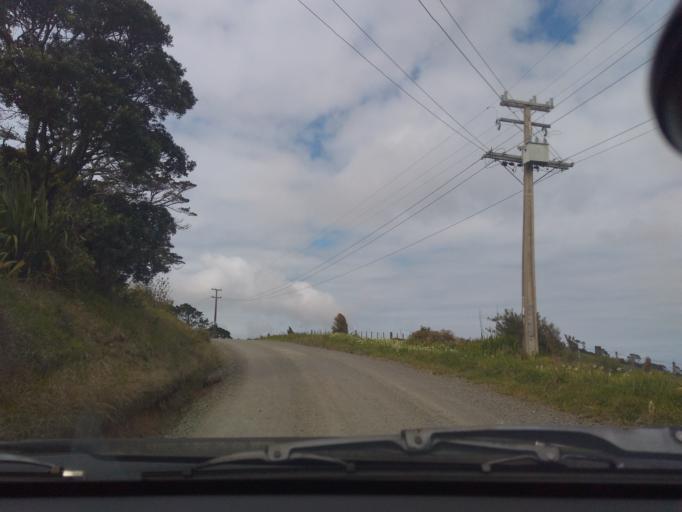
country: NZ
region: Auckland
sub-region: Auckland
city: Muriwai Beach
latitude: -36.8524
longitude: 174.4839
